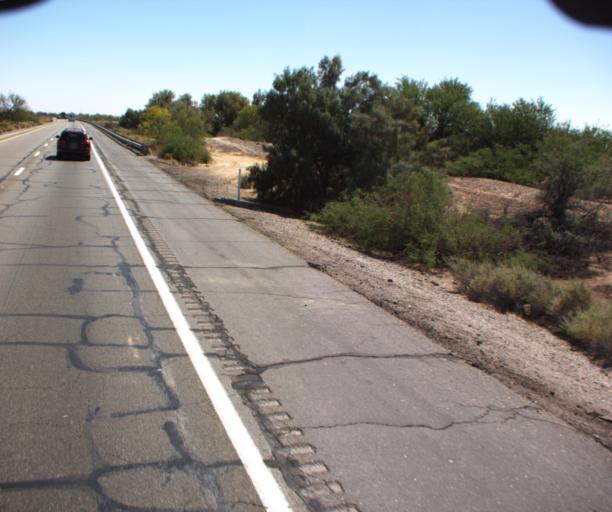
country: US
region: Arizona
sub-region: Yuma County
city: Wellton
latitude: 32.6501
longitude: -114.2155
